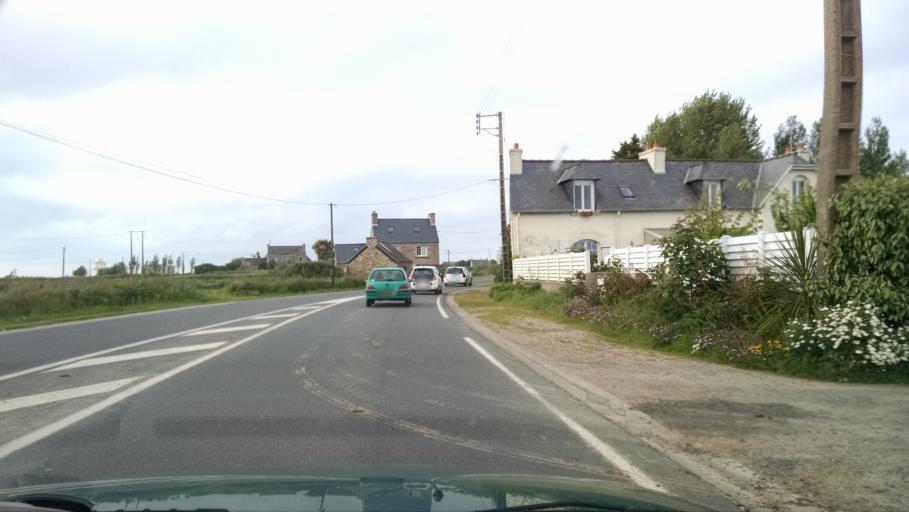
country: FR
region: Brittany
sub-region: Departement du Finistere
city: Roscoff
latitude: 48.7053
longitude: -3.9859
